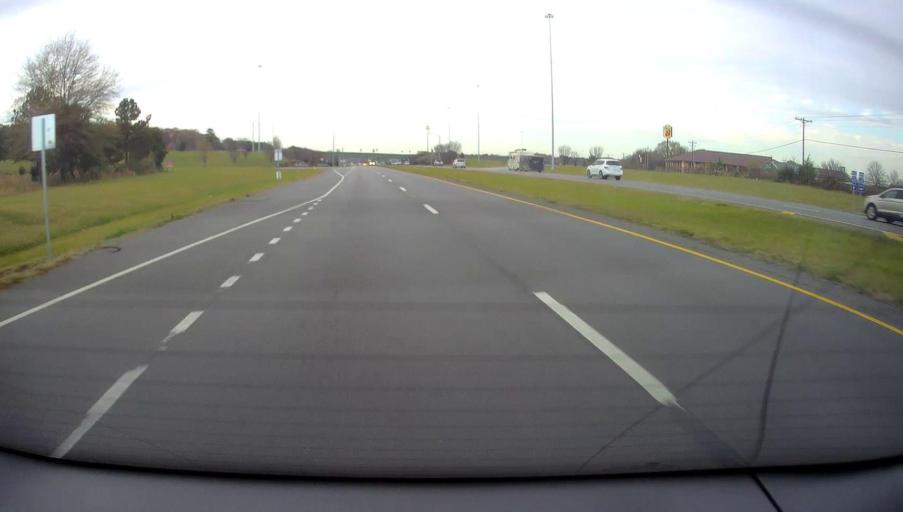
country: US
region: Alabama
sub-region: Morgan County
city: Priceville
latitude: 34.5310
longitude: -86.9027
